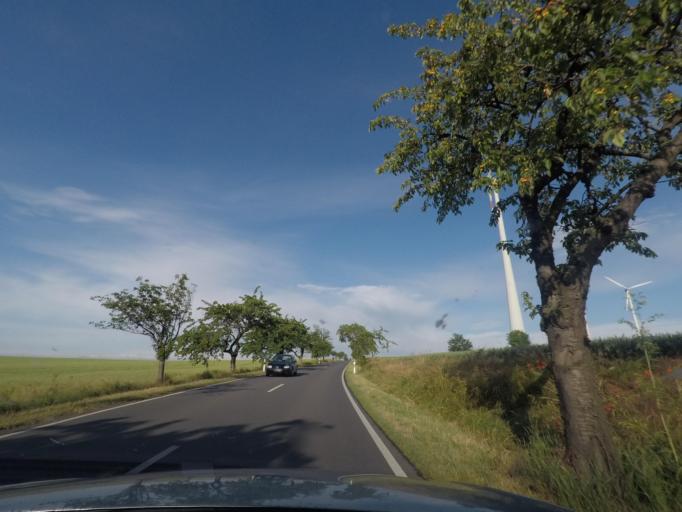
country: DE
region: Saxony-Anhalt
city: Huy-Neinstedt
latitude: 51.9798
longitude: 10.8680
